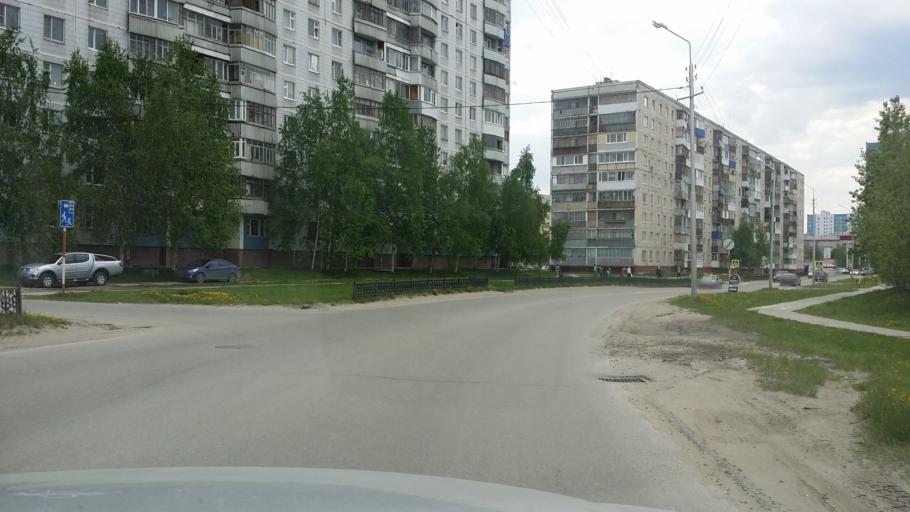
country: RU
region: Khanty-Mansiyskiy Avtonomnyy Okrug
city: Nizhnevartovsk
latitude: 60.9385
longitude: 76.6087
